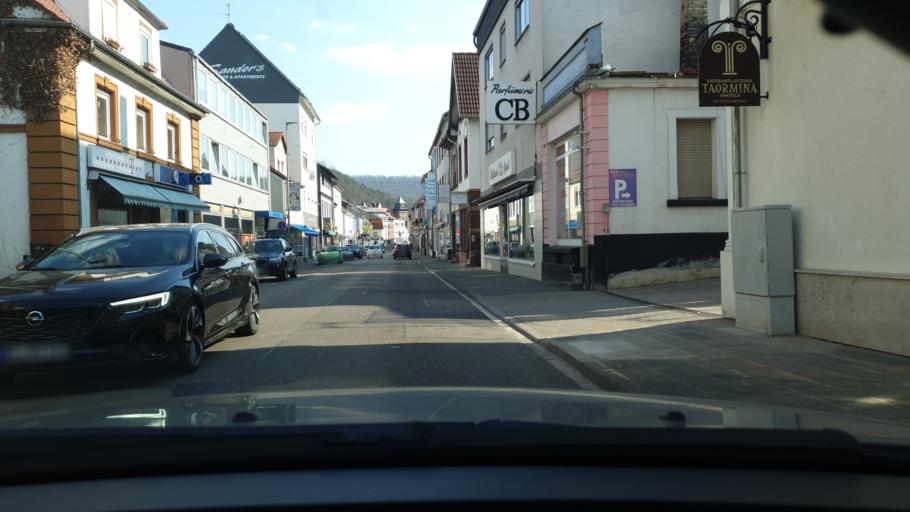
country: DE
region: Rheinland-Pfalz
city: Landstuhl
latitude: 49.4143
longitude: 7.5666
